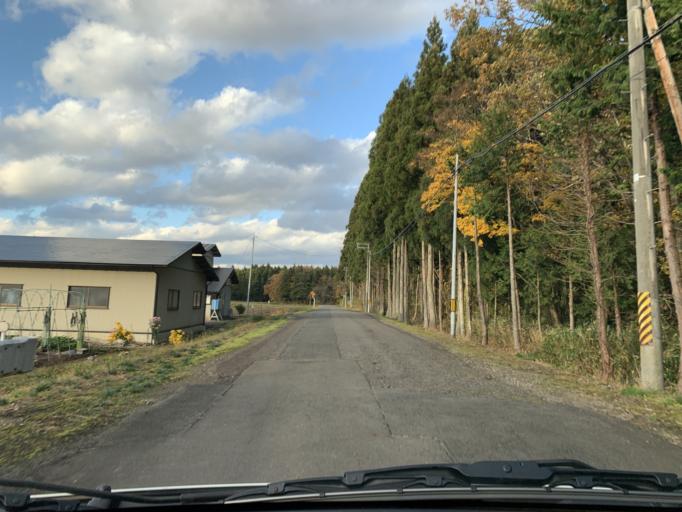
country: JP
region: Iwate
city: Mizusawa
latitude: 39.1187
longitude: 141.0269
